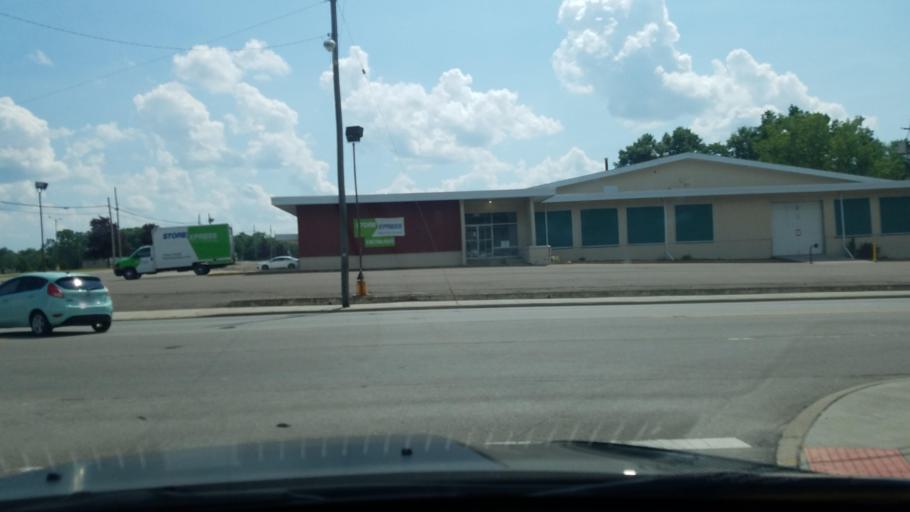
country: US
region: Ohio
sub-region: Trumbull County
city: Bolindale
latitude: 41.2202
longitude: -80.7796
